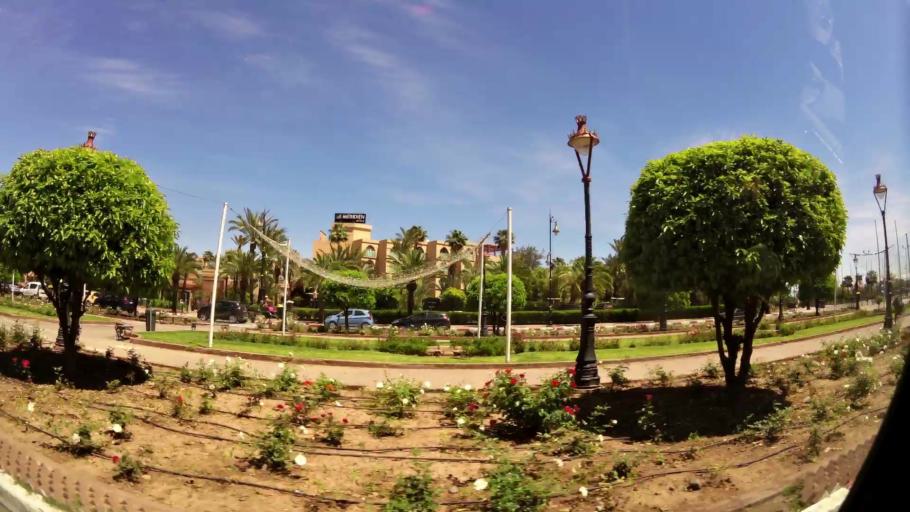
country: MA
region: Marrakech-Tensift-Al Haouz
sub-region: Marrakech
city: Marrakesh
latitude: 31.6185
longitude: -8.0086
